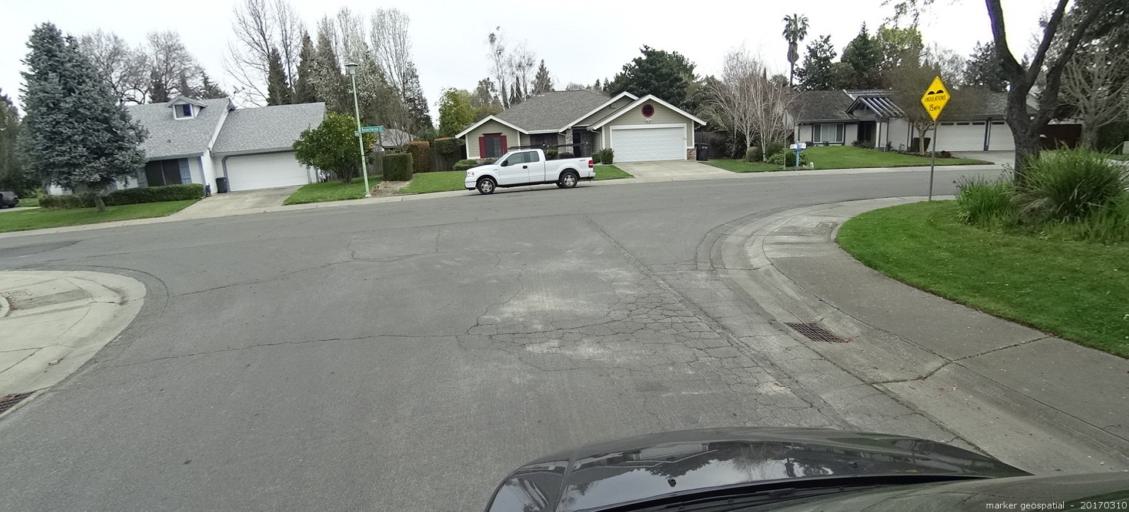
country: US
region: California
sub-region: Sacramento County
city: Parkway
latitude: 38.4854
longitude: -121.5234
